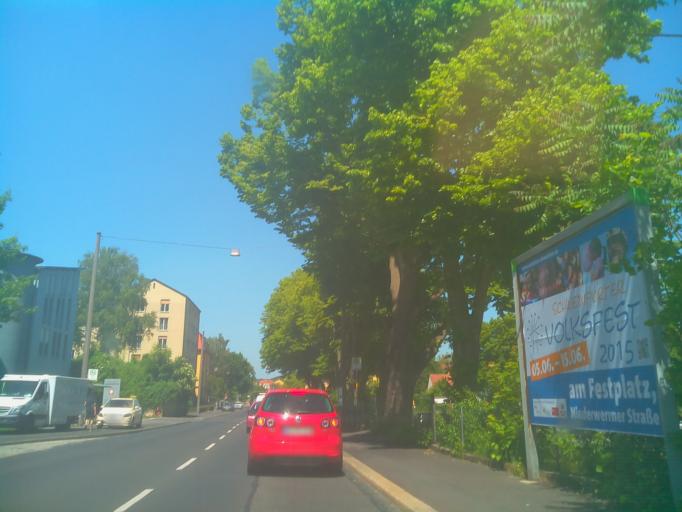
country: DE
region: Bavaria
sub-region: Regierungsbezirk Unterfranken
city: Schweinfurt
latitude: 50.0501
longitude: 10.2314
